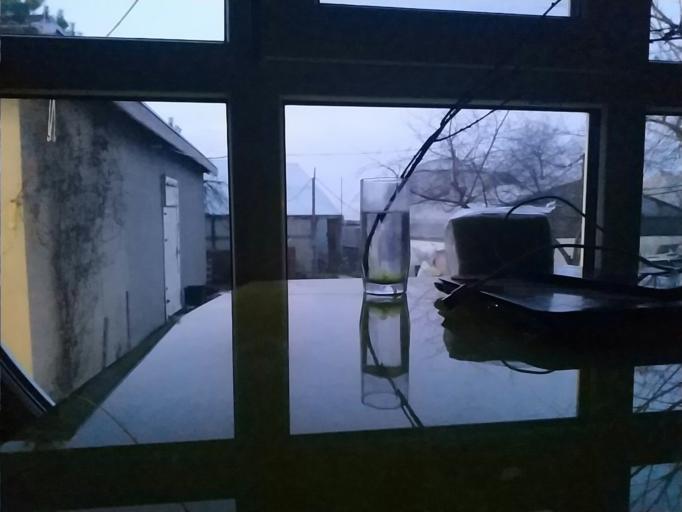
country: RU
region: Republic of Karelia
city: Sukkozero
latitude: 62.8278
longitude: 31.8313
